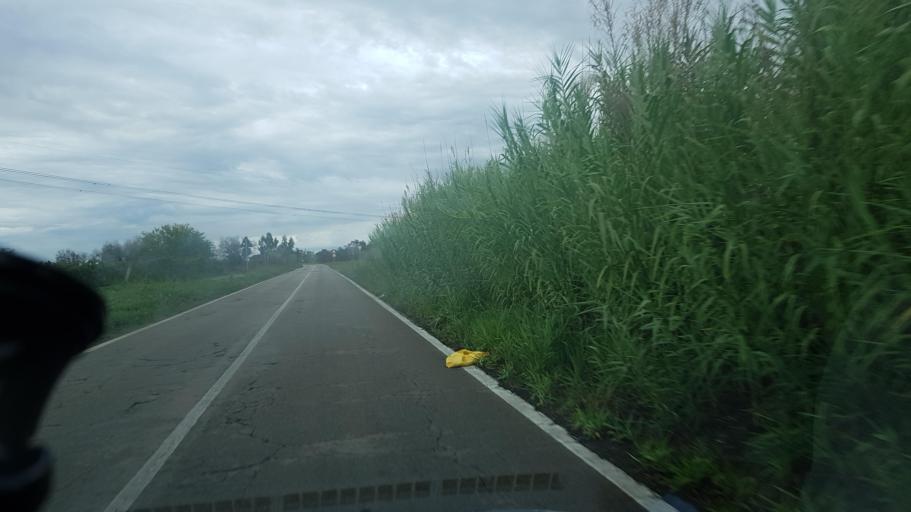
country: IT
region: Apulia
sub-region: Provincia di Lecce
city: Salice Salentino
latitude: 40.3672
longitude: 17.9956
